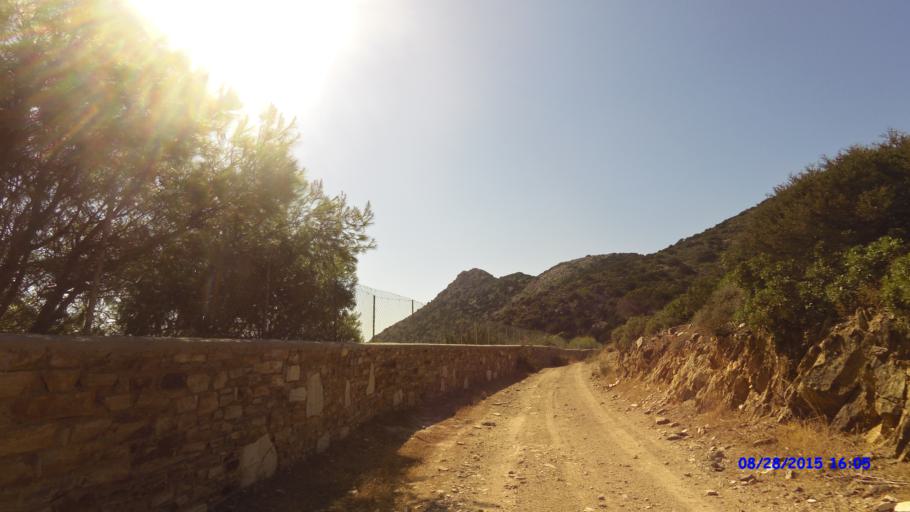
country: GR
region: South Aegean
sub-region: Nomos Kykladon
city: Antiparos
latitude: 37.0039
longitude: 25.0288
